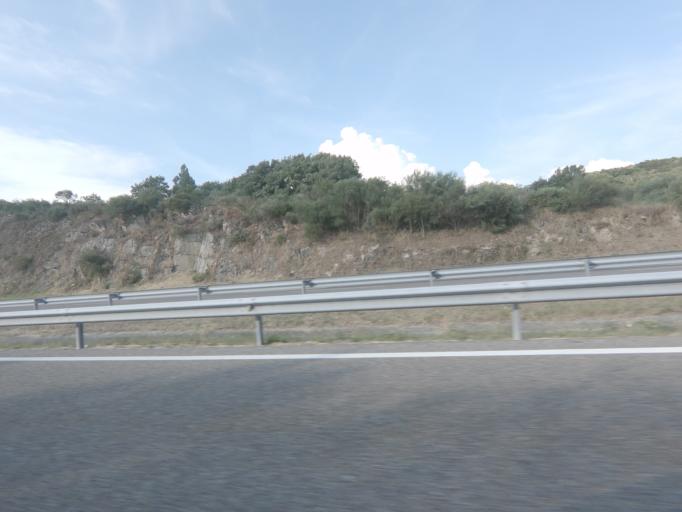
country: ES
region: Galicia
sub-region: Provincia de Ourense
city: Cualedro
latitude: 41.9918
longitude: -7.5578
